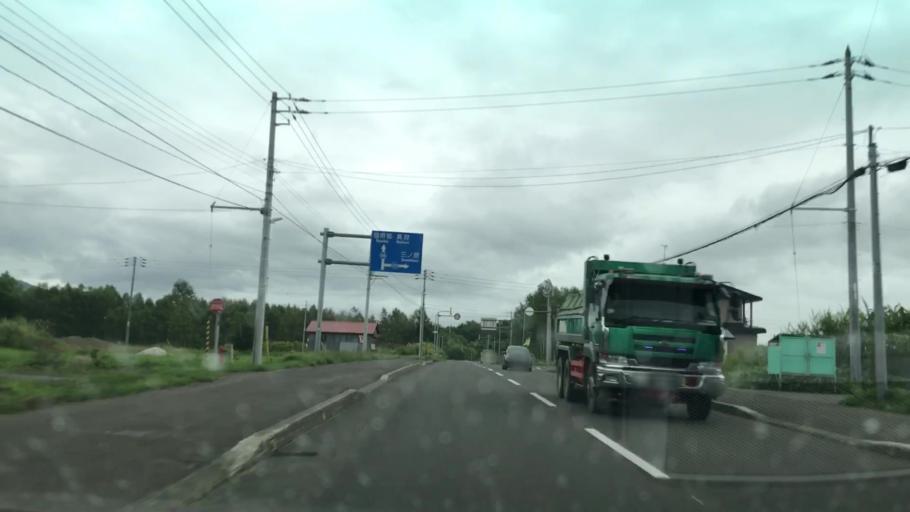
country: JP
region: Hokkaido
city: Niseko Town
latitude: 42.7962
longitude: 140.7120
